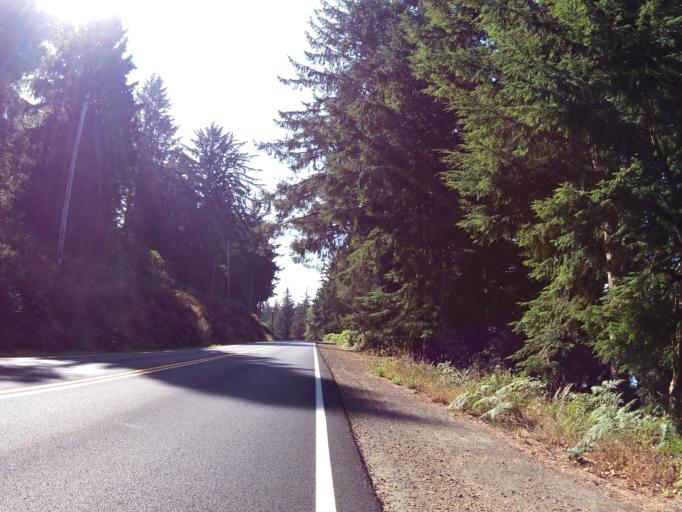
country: US
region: Oregon
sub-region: Tillamook County
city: Pacific City
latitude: 45.2724
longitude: -123.9457
